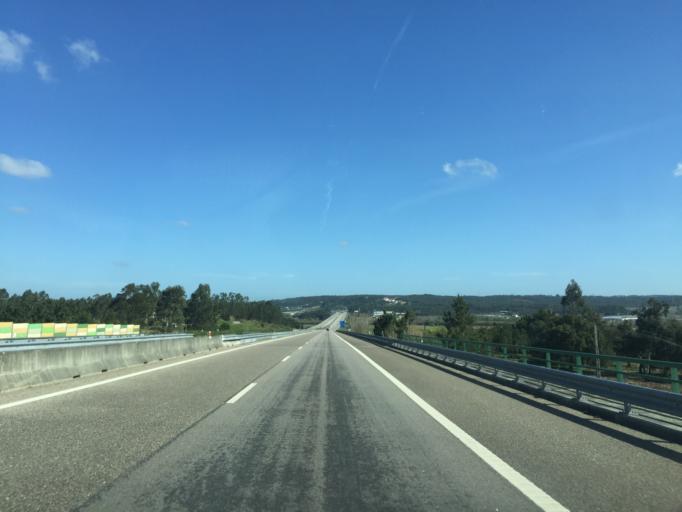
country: PT
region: Leiria
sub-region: Leiria
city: Amor
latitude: 39.7963
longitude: -8.8557
